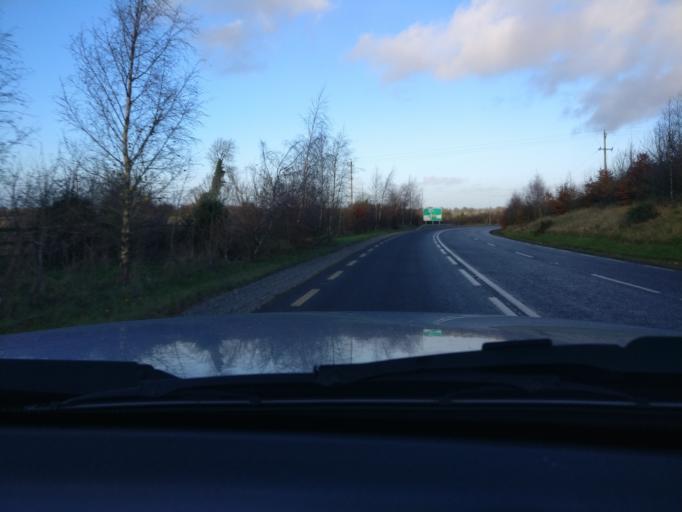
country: IE
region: Leinster
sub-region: An Mhi
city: Kells
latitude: 53.7359
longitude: -6.8891
